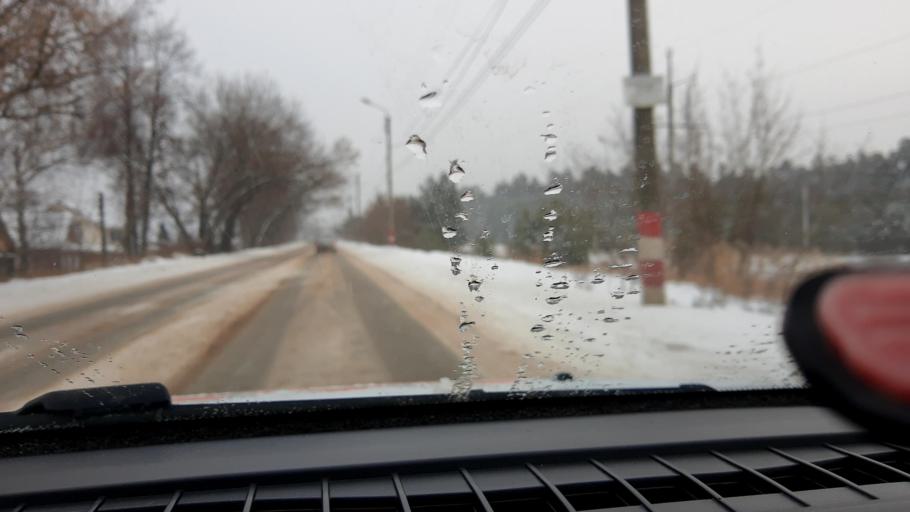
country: RU
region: Nizjnij Novgorod
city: Bor
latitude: 56.3282
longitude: 44.1272
